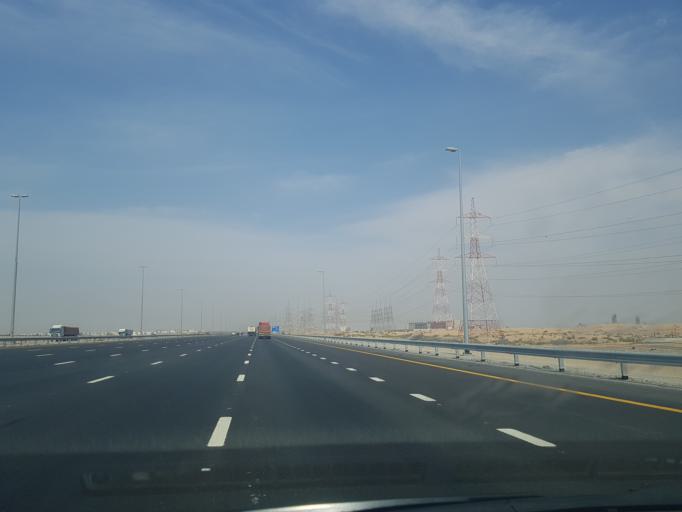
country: AE
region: Ash Shariqah
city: Sharjah
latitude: 25.2782
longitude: 55.5850
